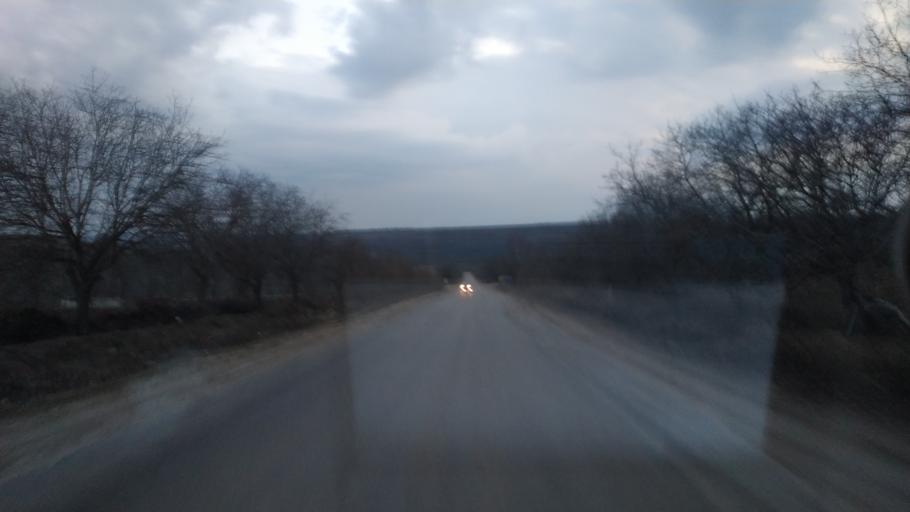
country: MD
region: Anenii Noi
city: Anenii Noi
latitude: 46.9592
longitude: 29.2839
